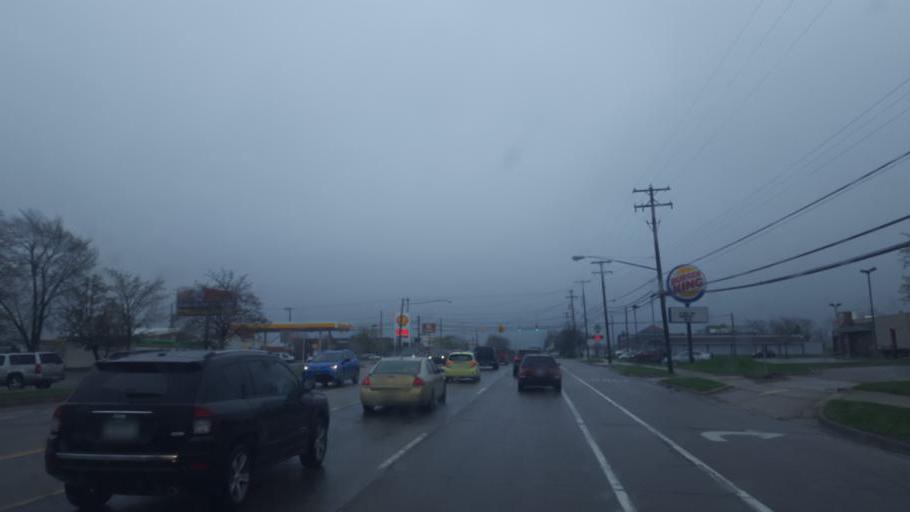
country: US
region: Michigan
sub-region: Isabella County
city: Mount Pleasant
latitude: 43.5838
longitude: -84.7676
